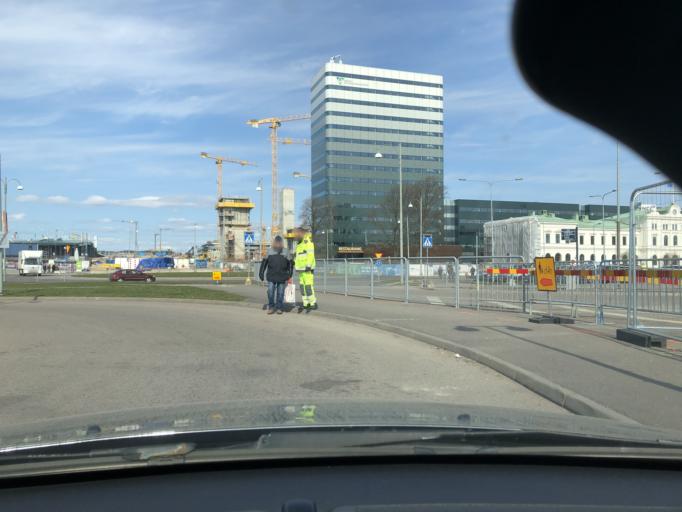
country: SE
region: Vaestra Goetaland
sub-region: Goteborg
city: Goeteborg
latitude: 57.7108
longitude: 11.9731
